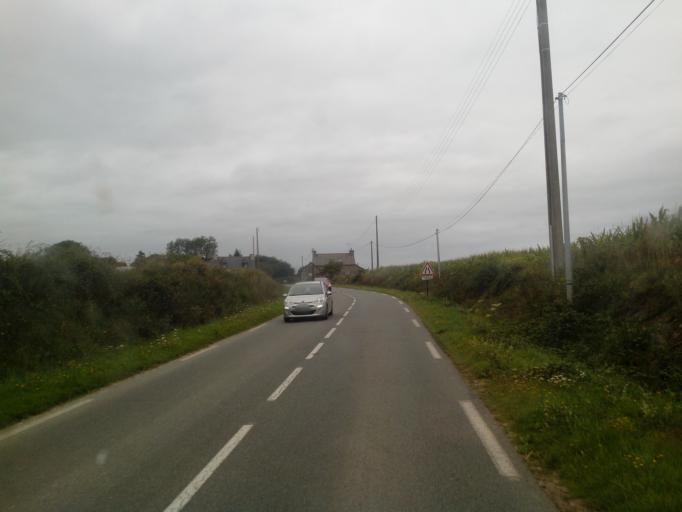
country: FR
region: Brittany
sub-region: Departement des Cotes-d'Armor
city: Plouezec
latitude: 48.7322
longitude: -2.9820
